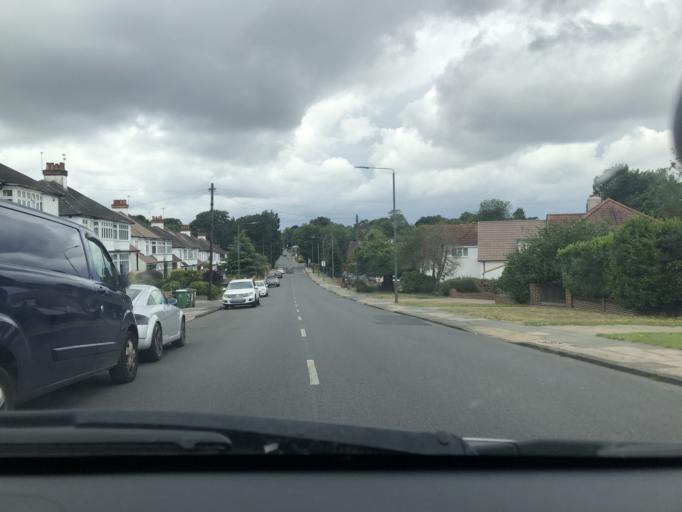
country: GB
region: England
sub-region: Greater London
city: Bexley
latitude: 51.4439
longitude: 0.1379
